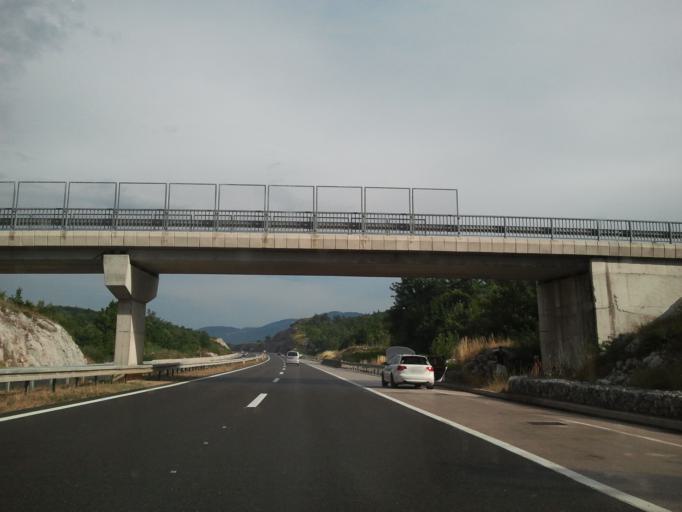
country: HR
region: Zadarska
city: Obrovac
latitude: 44.3410
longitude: 15.6486
